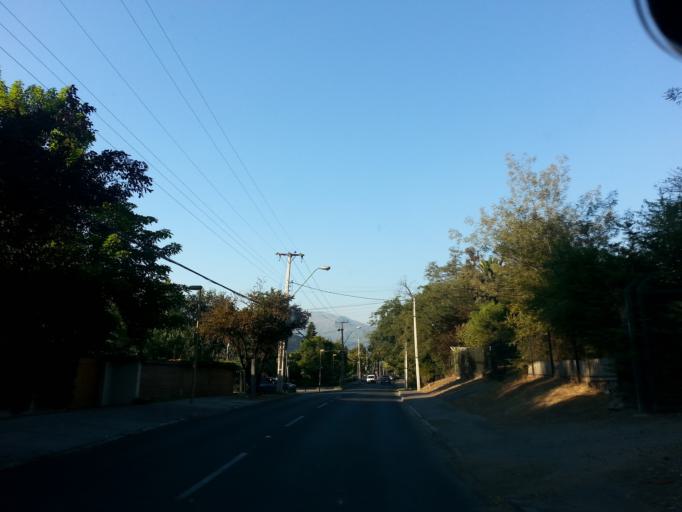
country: CL
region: Santiago Metropolitan
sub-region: Provincia de Santiago
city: Villa Presidente Frei, Nunoa, Santiago, Chile
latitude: -33.3941
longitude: -70.5395
